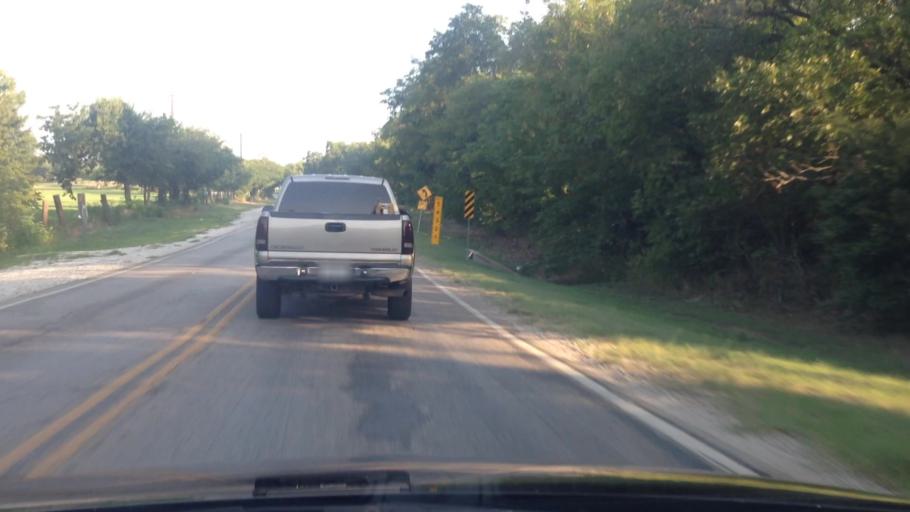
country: US
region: Texas
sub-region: Tarrant County
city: Rendon
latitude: 32.6021
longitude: -97.2644
